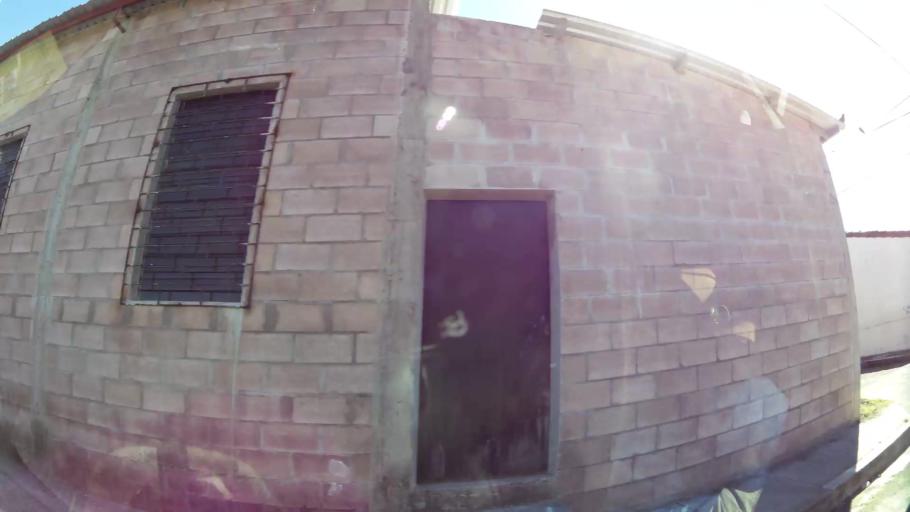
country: SV
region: San Miguel
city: San Miguel
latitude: 13.4921
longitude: -88.1659
